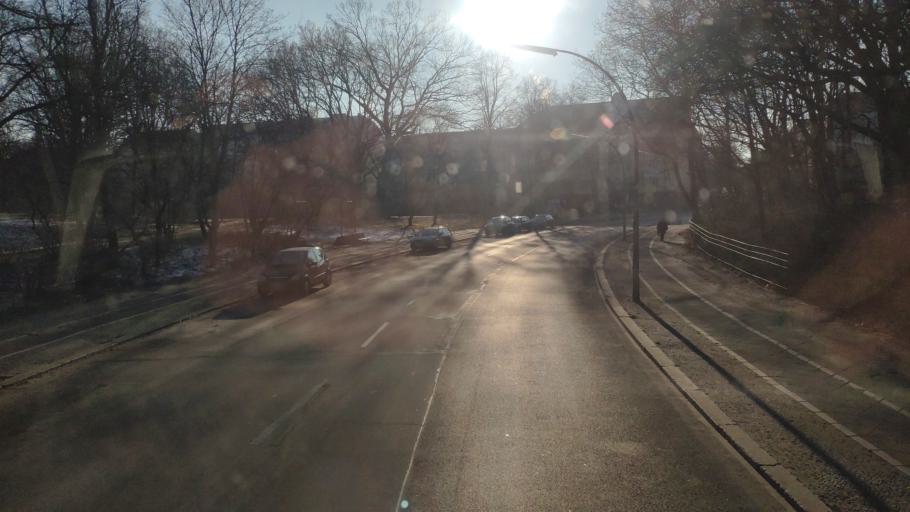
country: DE
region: Berlin
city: Wedding Bezirk
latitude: 52.5571
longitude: 13.3495
